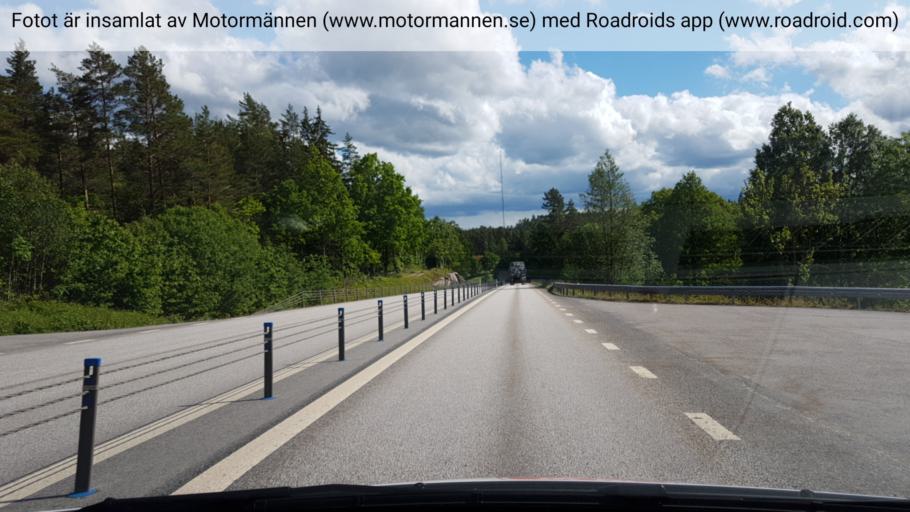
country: SE
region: Kalmar
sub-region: Vasterviks Kommun
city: Gamleby
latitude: 57.8566
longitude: 16.4292
